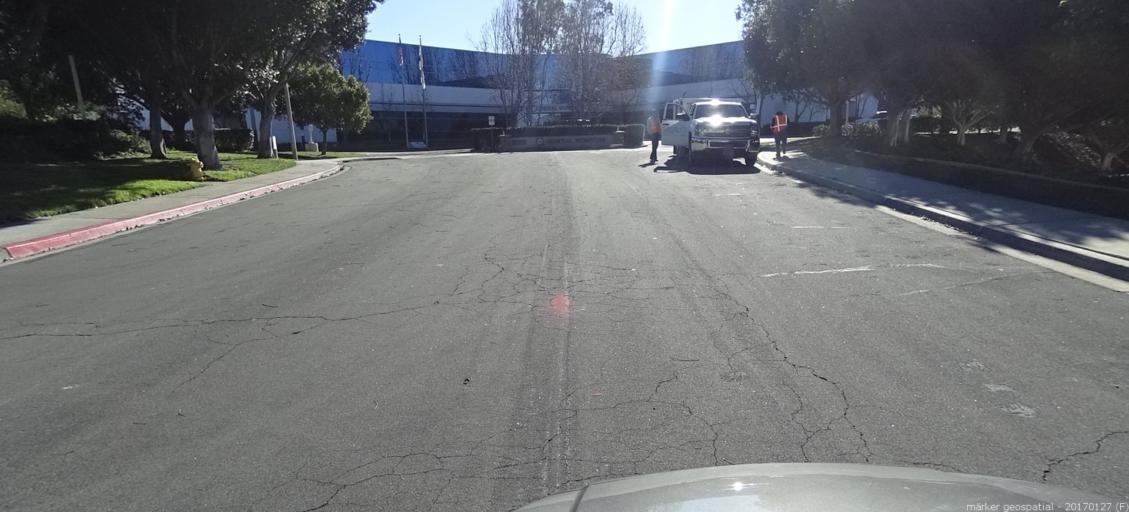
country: US
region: California
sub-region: Orange County
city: Foothill Ranch
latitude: 33.6641
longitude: -117.6636
